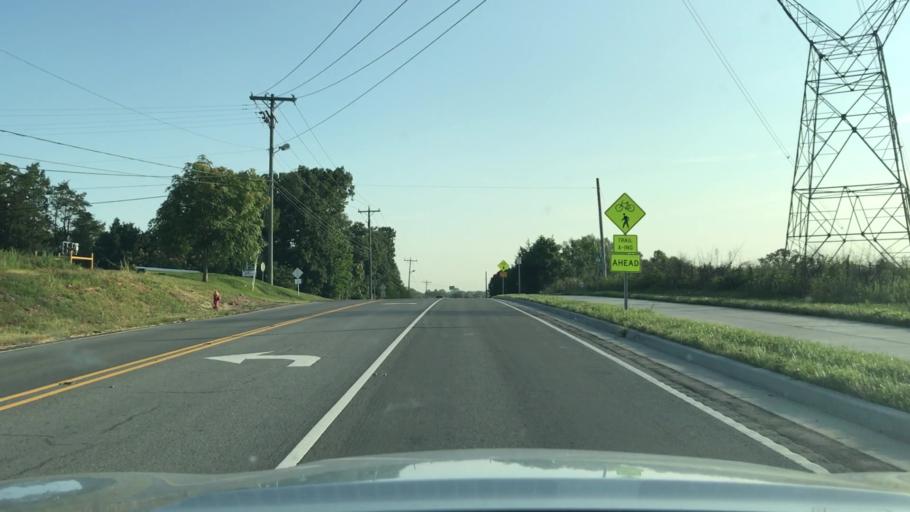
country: US
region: Tennessee
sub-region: Rutherford County
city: La Vergne
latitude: 36.0548
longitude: -86.5989
